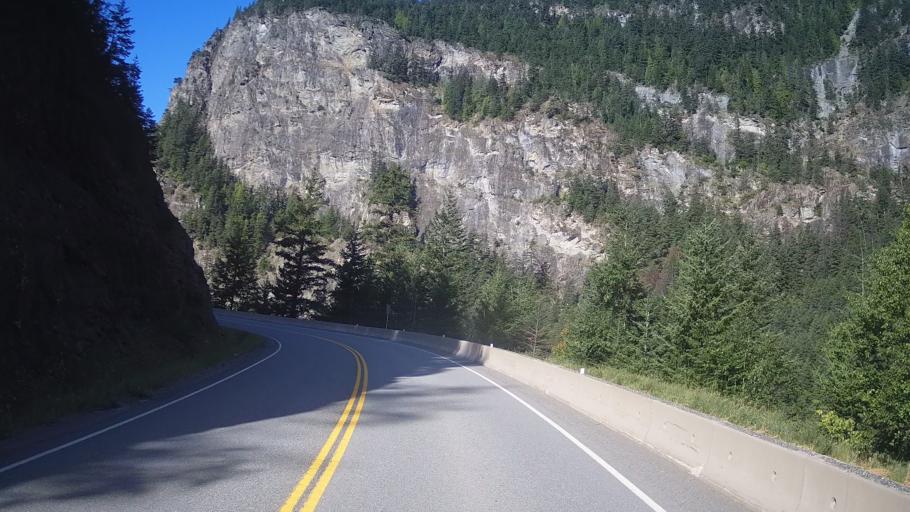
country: CA
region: British Columbia
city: Lillooet
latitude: 50.6463
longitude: -122.0690
